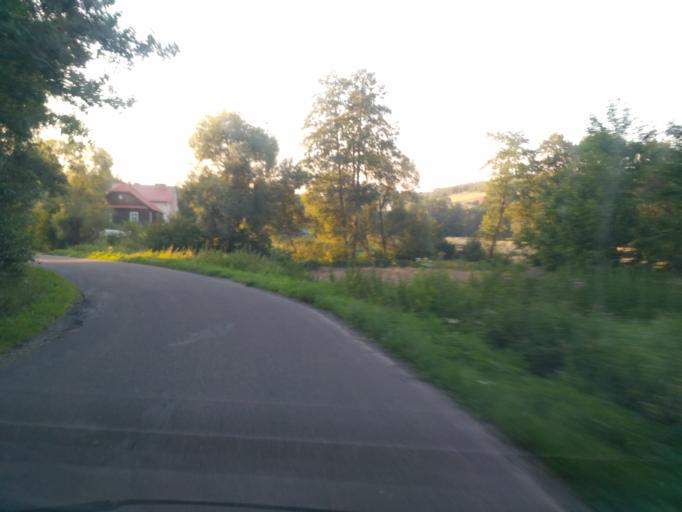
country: PL
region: Subcarpathian Voivodeship
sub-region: Powiat strzyzowski
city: Wysoka Strzyzowska
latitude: 49.8061
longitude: 21.7473
